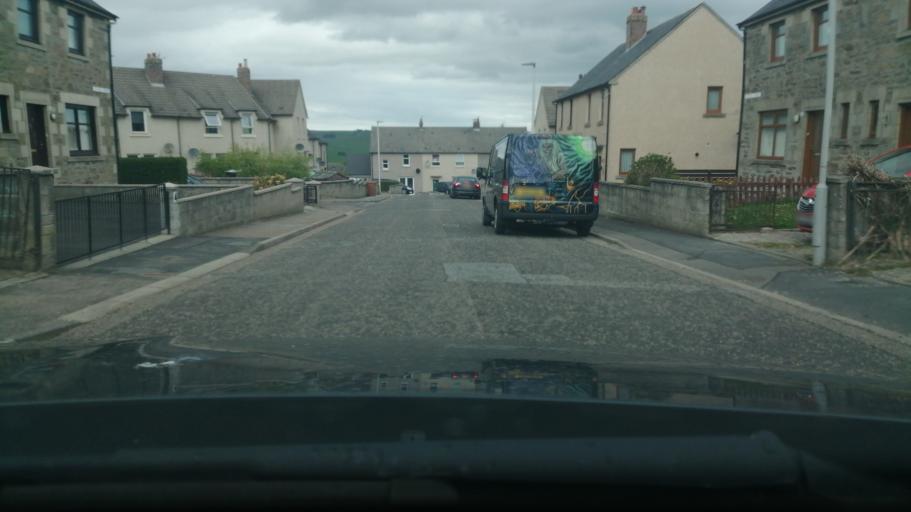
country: GB
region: Scotland
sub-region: Moray
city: Keith
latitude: 57.5402
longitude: -2.9551
